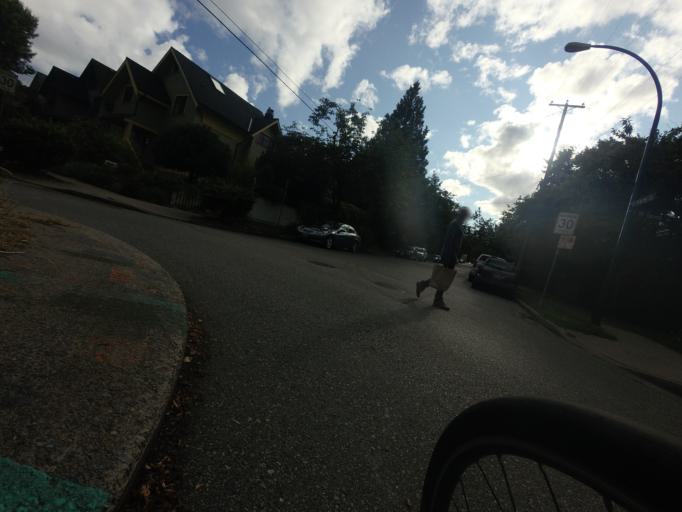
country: CA
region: British Columbia
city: West End
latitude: 49.2655
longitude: -123.1481
